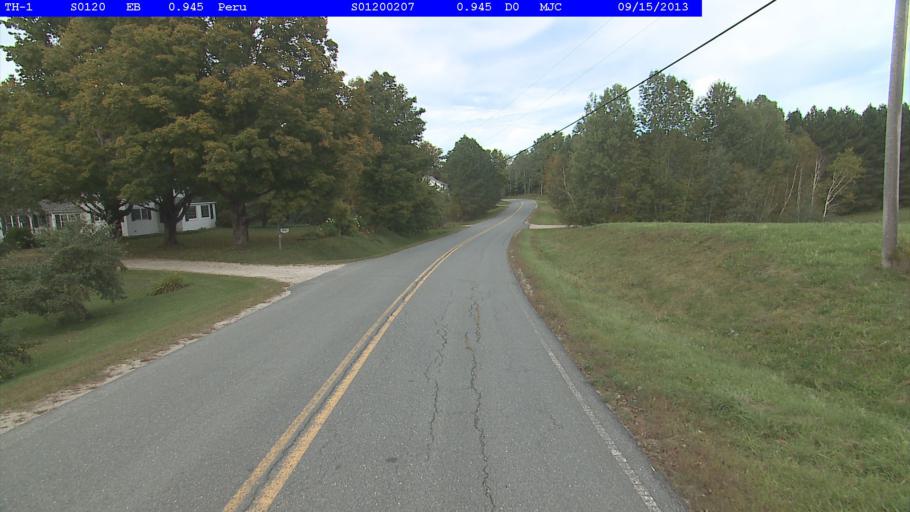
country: US
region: Vermont
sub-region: Bennington County
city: Manchester Center
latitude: 43.2392
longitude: -72.8966
